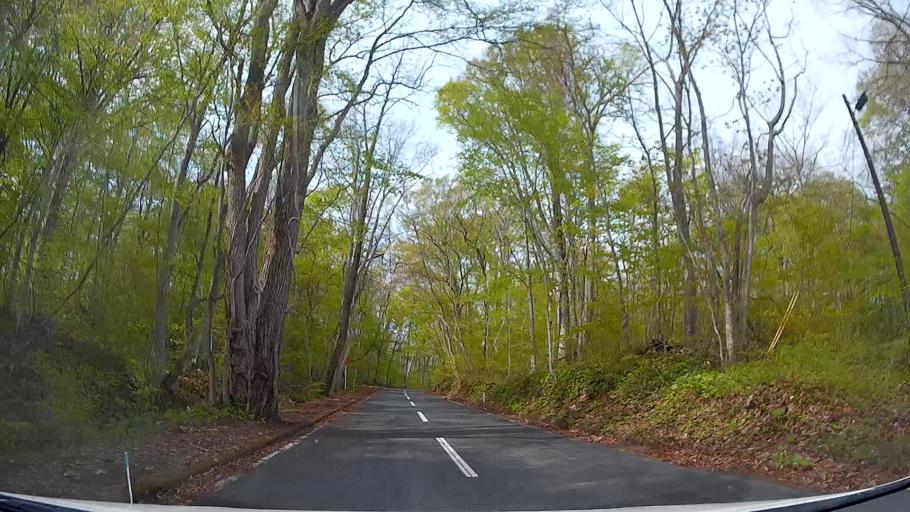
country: JP
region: Akita
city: Hanawa
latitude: 40.4326
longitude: 140.9154
